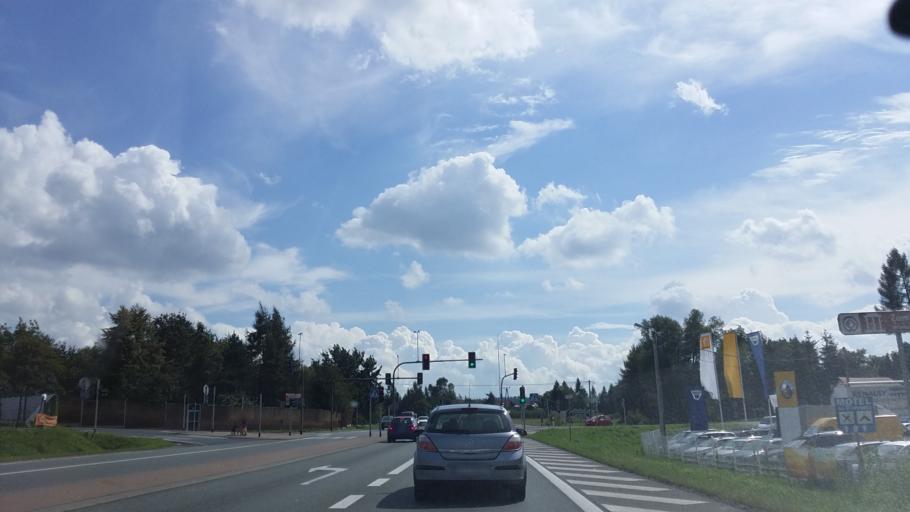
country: PL
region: Lesser Poland Voivodeship
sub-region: Powiat wielicki
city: Wieliczka
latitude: 49.9906
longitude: 20.0807
